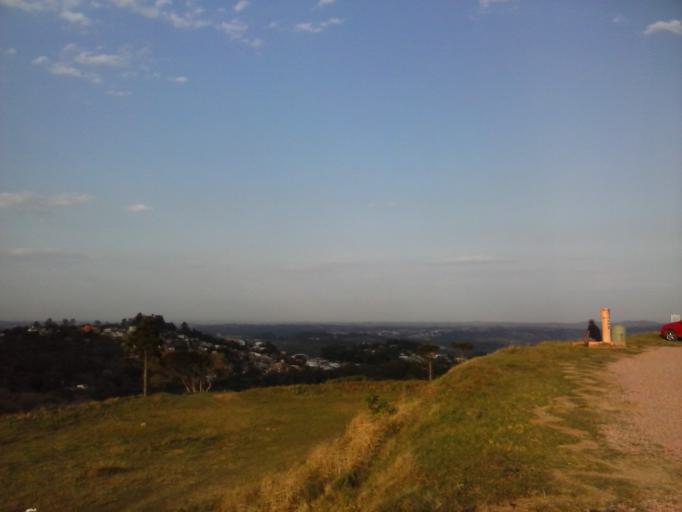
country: BR
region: Rio Grande do Sul
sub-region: Porto Alegre
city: Porto Alegre
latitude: -30.0991
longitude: -51.1820
